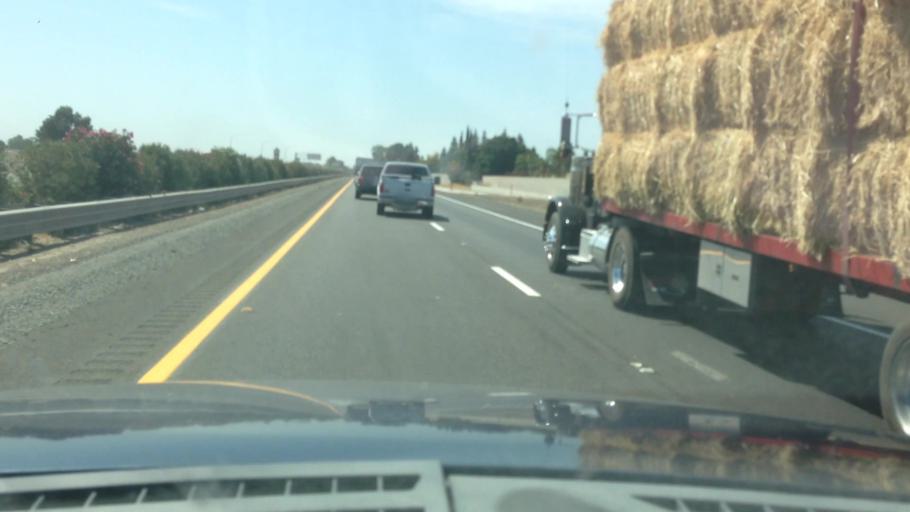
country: US
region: California
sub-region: Tulare County
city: Tulare
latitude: 36.2364
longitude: -119.3398
